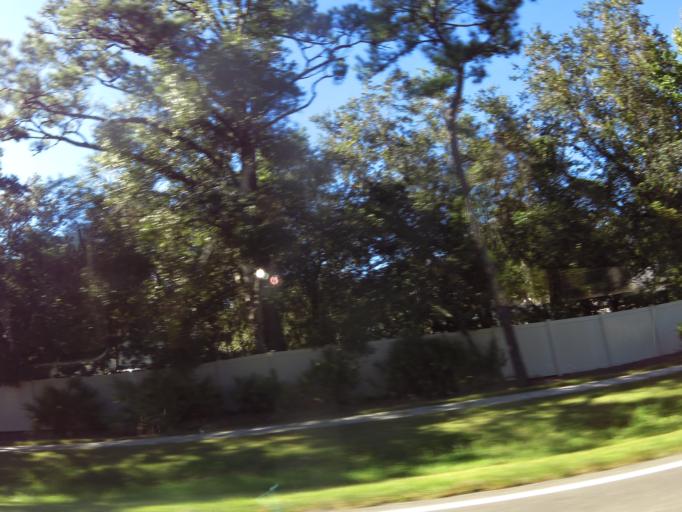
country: US
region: Florida
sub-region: Saint Johns County
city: Palm Valley
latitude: 30.1411
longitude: -81.3785
